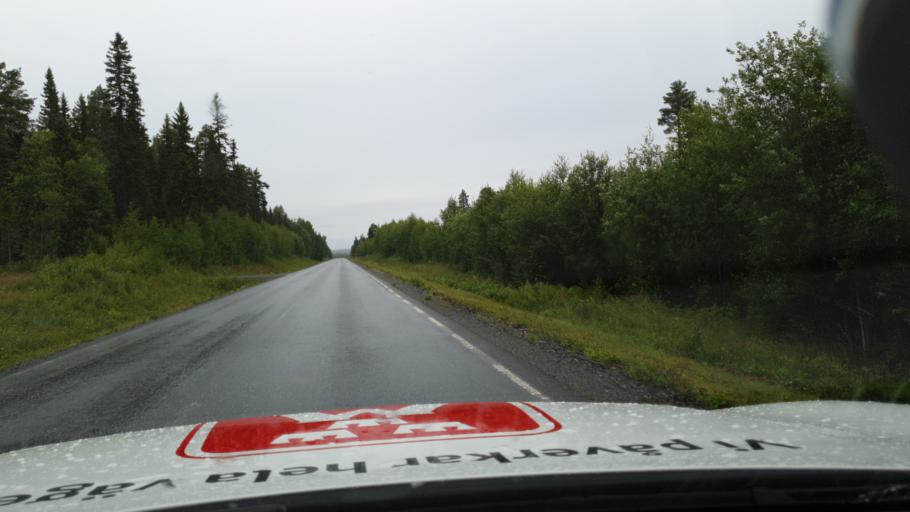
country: SE
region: Jaemtland
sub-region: Krokoms Kommun
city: Krokom
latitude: 63.3086
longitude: 14.4264
